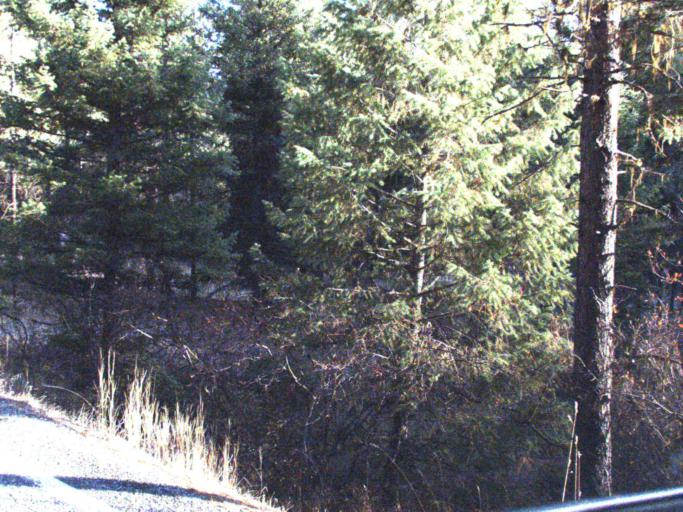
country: US
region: Washington
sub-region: Ferry County
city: Republic
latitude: 48.3797
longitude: -118.7482
